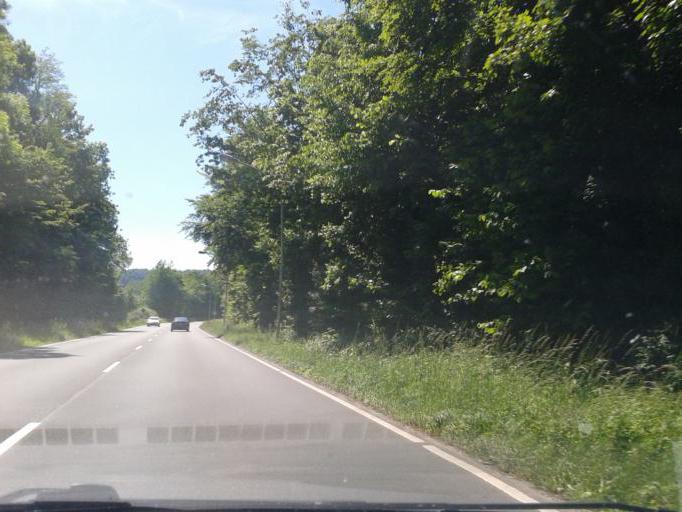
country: DE
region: North Rhine-Westphalia
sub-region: Regierungsbezirk Detmold
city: Bad Meinberg
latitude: 51.9185
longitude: 9.0299
